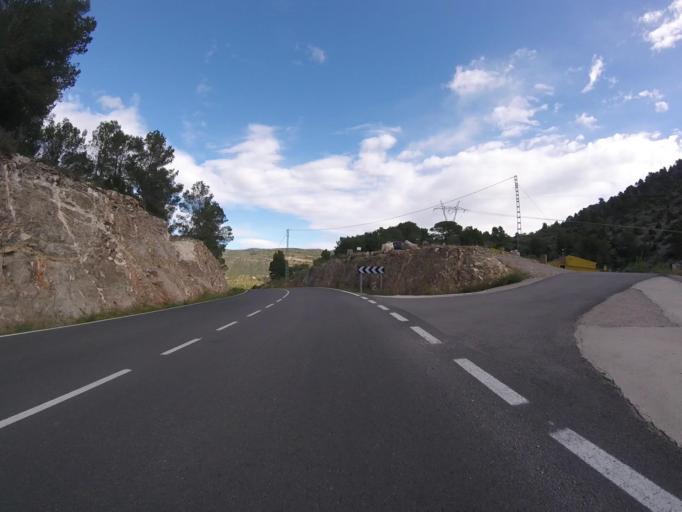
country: ES
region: Valencia
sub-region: Provincia de Castello
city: Culla
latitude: 40.2741
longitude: -0.1103
